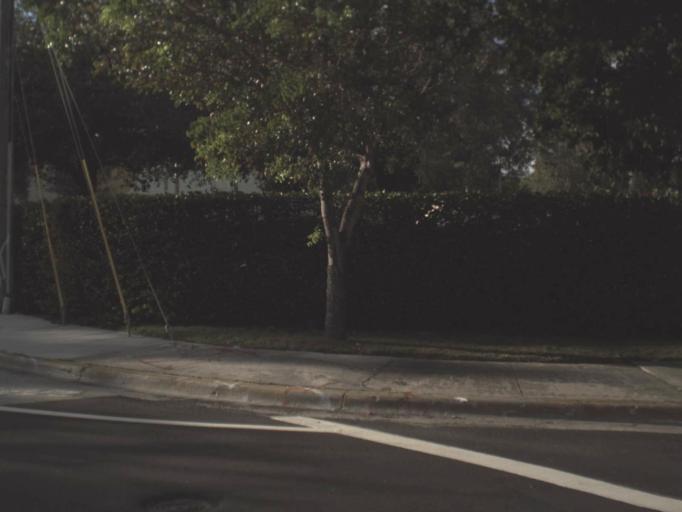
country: US
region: Florida
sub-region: Miami-Dade County
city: South Miami
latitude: 25.7061
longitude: -80.2920
